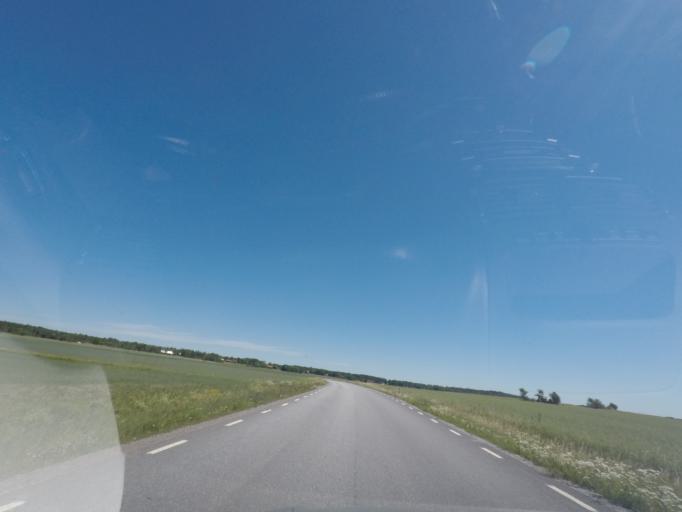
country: SE
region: Uppsala
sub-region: Enkopings Kommun
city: Enkoping
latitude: 59.7096
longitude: 17.0464
